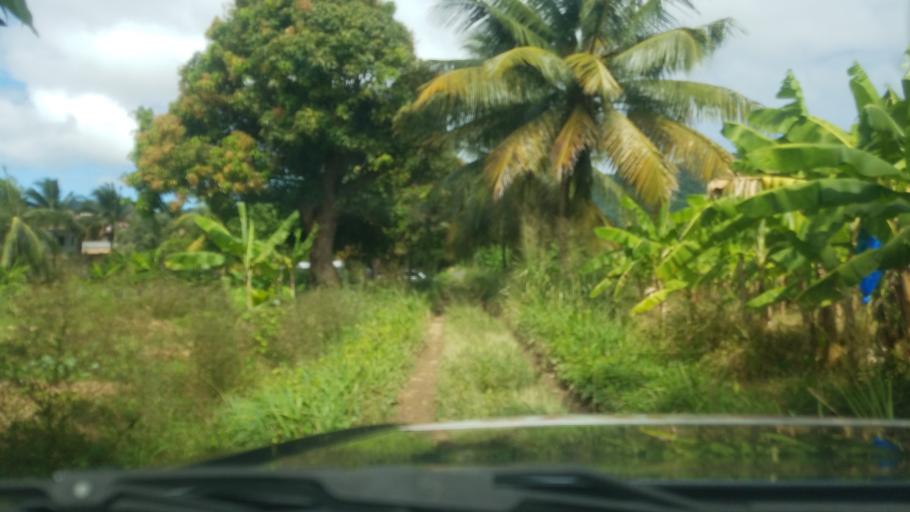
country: LC
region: Dennery Quarter
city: Dennery
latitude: 13.9359
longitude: -60.9177
